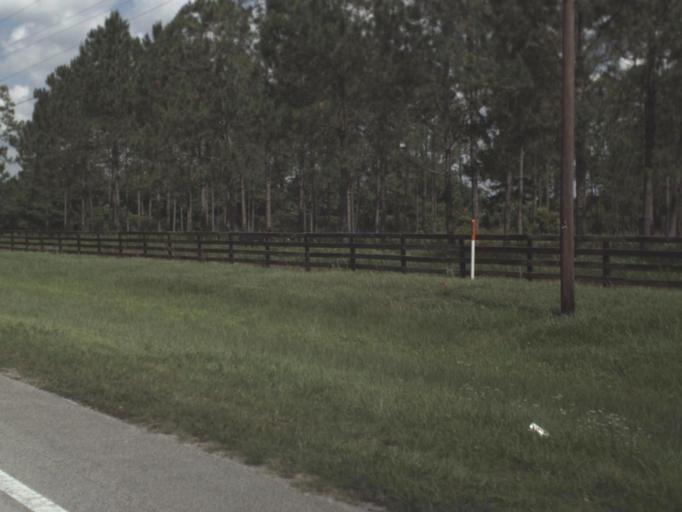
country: US
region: Florida
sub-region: Putnam County
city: East Palatka
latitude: 29.7257
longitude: -81.4510
